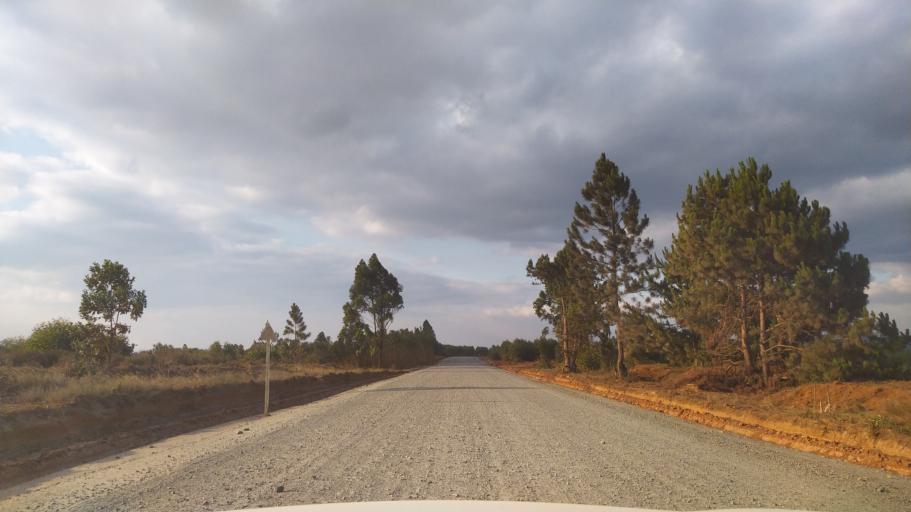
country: MG
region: Analamanga
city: Anjozorobe
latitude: -18.5216
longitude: 48.2624
